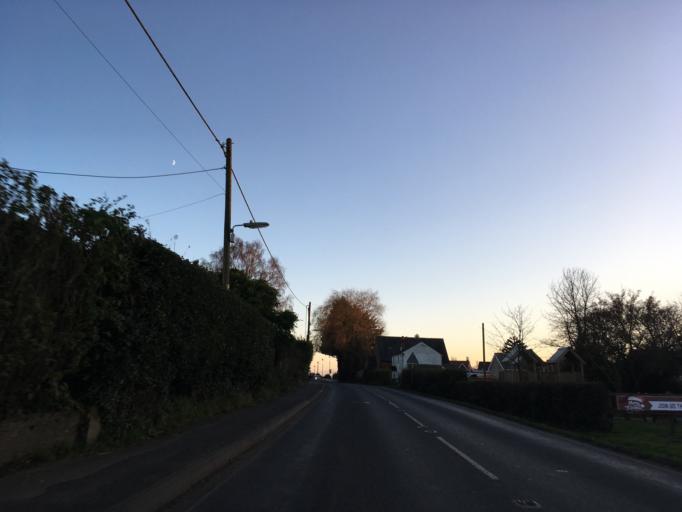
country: GB
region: England
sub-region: Hampshire
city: Colden Common
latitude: 50.9759
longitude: -1.3027
